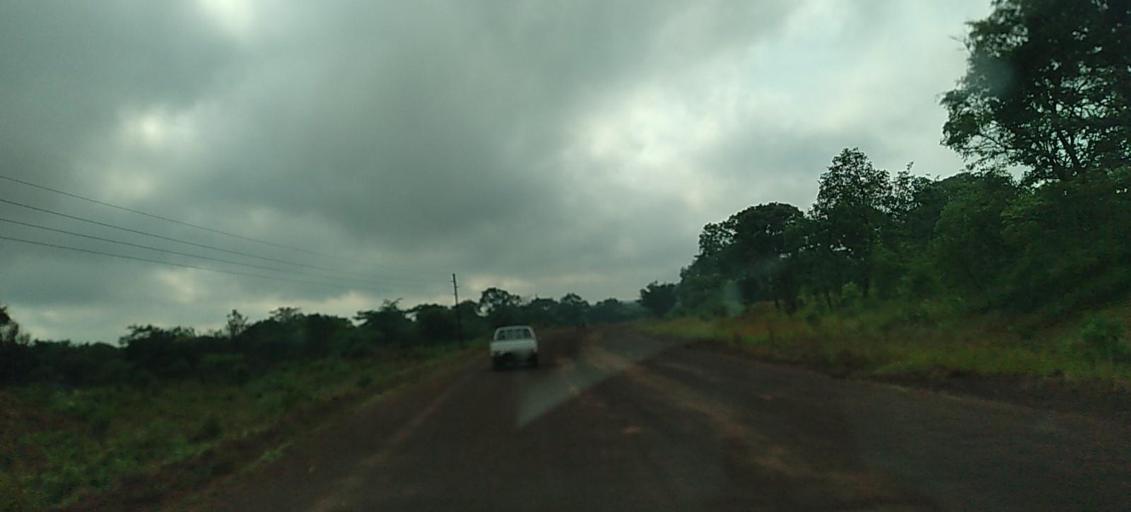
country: ZM
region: North-Western
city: Mwinilunga
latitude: -11.7258
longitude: 24.5752
